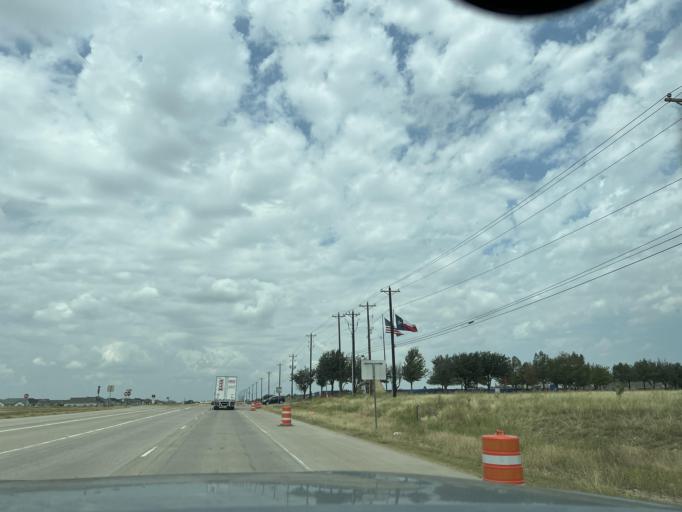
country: US
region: Texas
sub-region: Denton County
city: Justin
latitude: 33.0354
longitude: -97.3287
